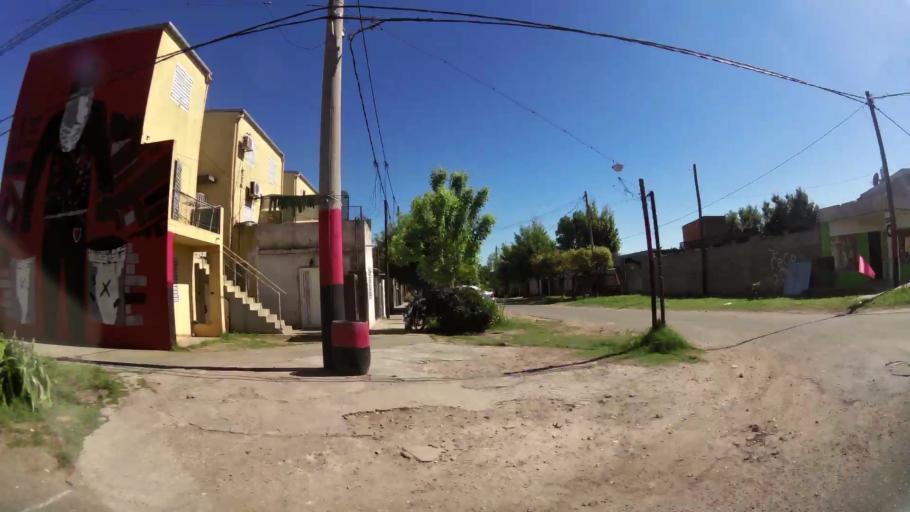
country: AR
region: Santa Fe
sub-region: Departamento de Rosario
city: Rosario
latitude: -32.9682
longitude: -60.6976
